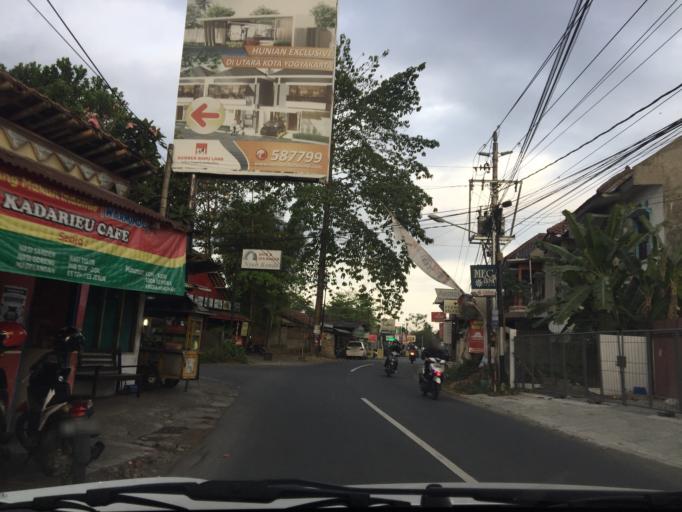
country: ID
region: Daerah Istimewa Yogyakarta
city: Melati
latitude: -7.7342
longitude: 110.3925
